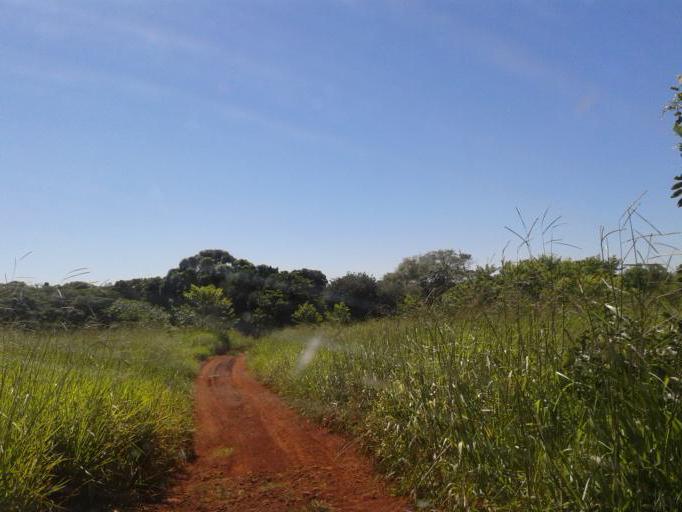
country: BR
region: Minas Gerais
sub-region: Capinopolis
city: Capinopolis
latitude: -18.6665
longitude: -49.5987
